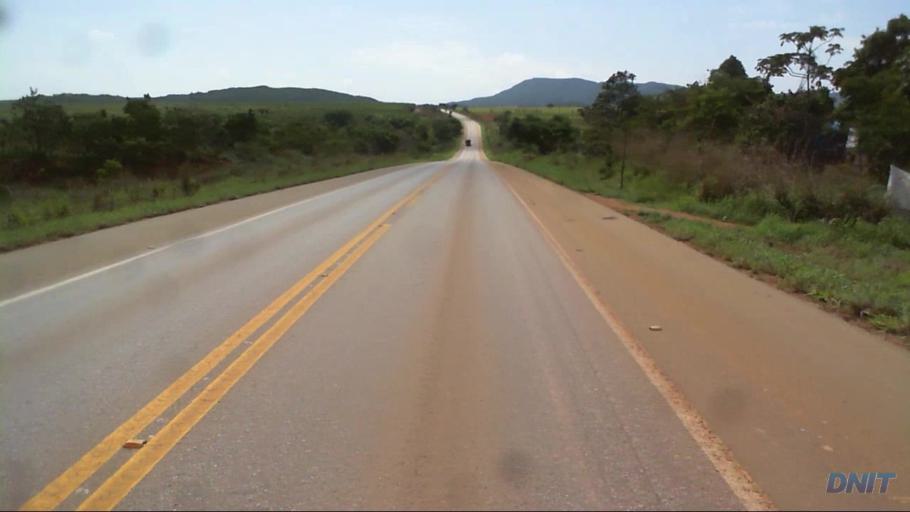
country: BR
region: Goias
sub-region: Barro Alto
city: Barro Alto
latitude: -15.1887
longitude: -48.7774
